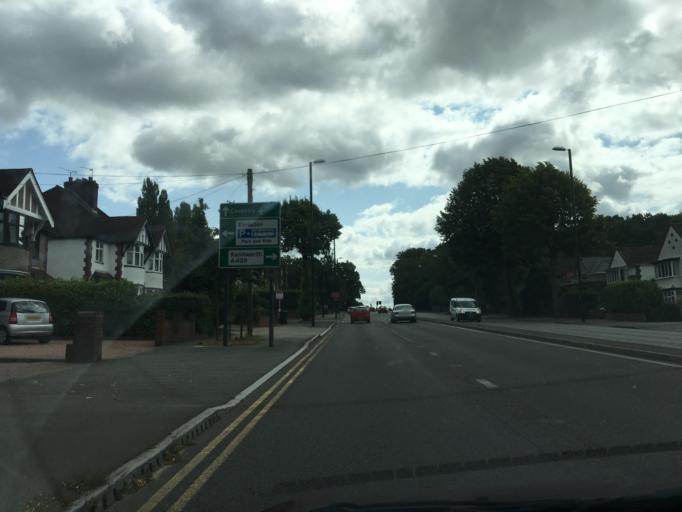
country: GB
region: England
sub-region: Coventry
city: Coventry
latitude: 52.3876
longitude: -1.5383
